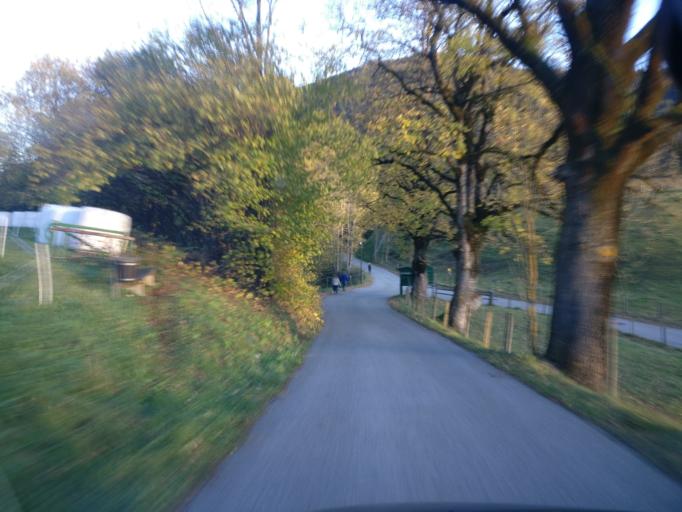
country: AT
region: Salzburg
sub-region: Politischer Bezirk Zell am See
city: Lend
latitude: 47.3147
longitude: 13.0371
